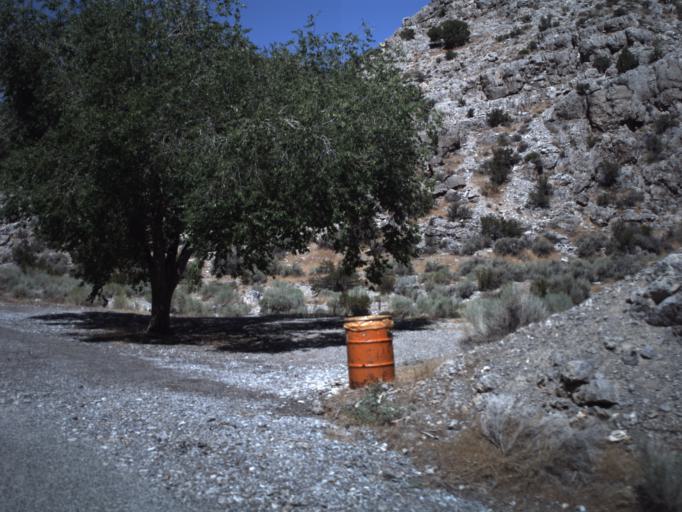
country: US
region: Utah
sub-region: Beaver County
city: Milford
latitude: 39.0843
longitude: -113.5722
